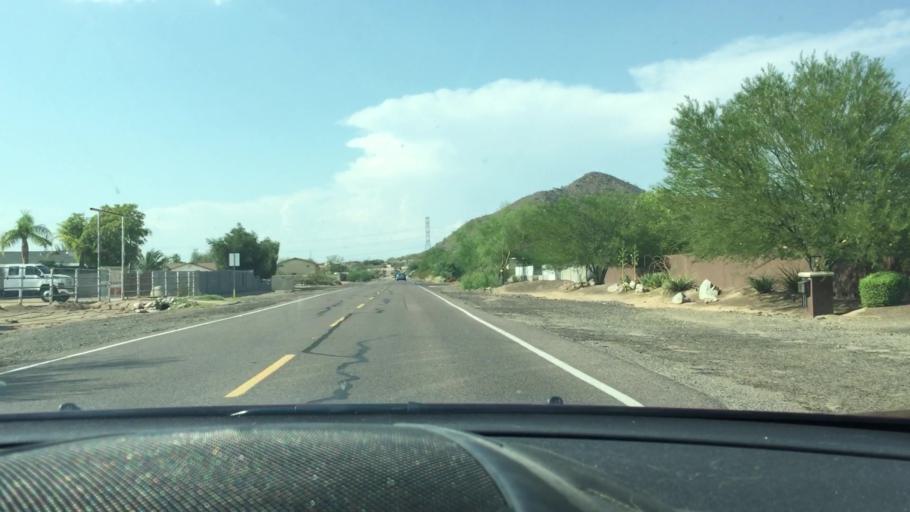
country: US
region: Arizona
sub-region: Maricopa County
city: Sun City West
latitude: 33.7025
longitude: -112.2550
